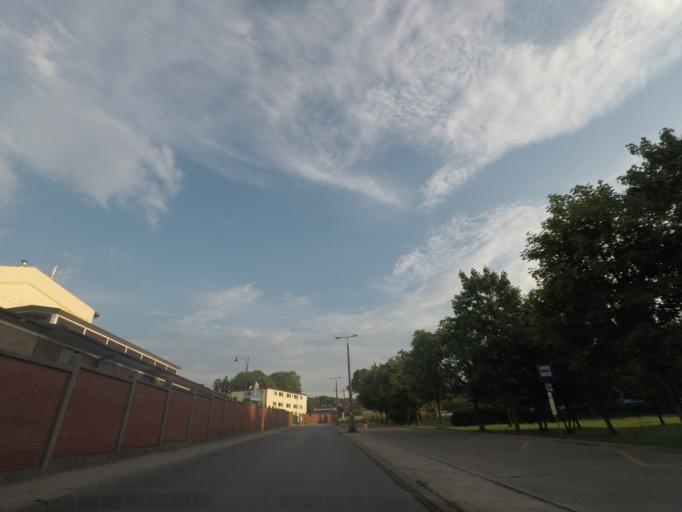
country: PL
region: Lesser Poland Voivodeship
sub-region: Powiat wielicki
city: Wieliczka
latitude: 49.9858
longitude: 20.0506
